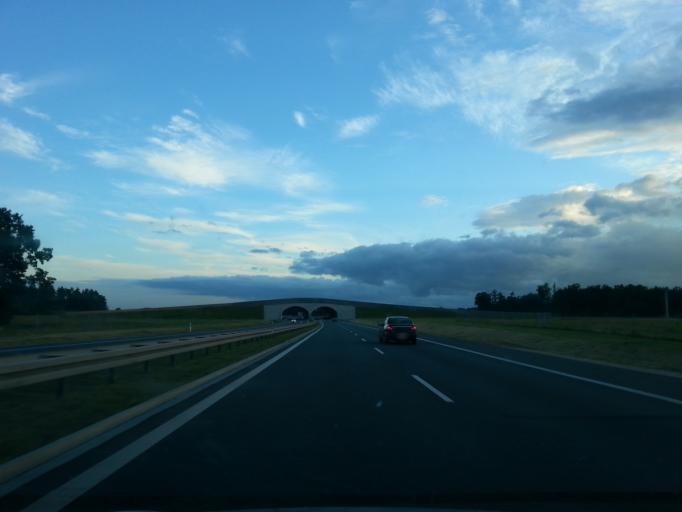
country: PL
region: Lower Silesian Voivodeship
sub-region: Powiat olesnicki
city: Twardogora
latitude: 51.2765
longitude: 17.5613
